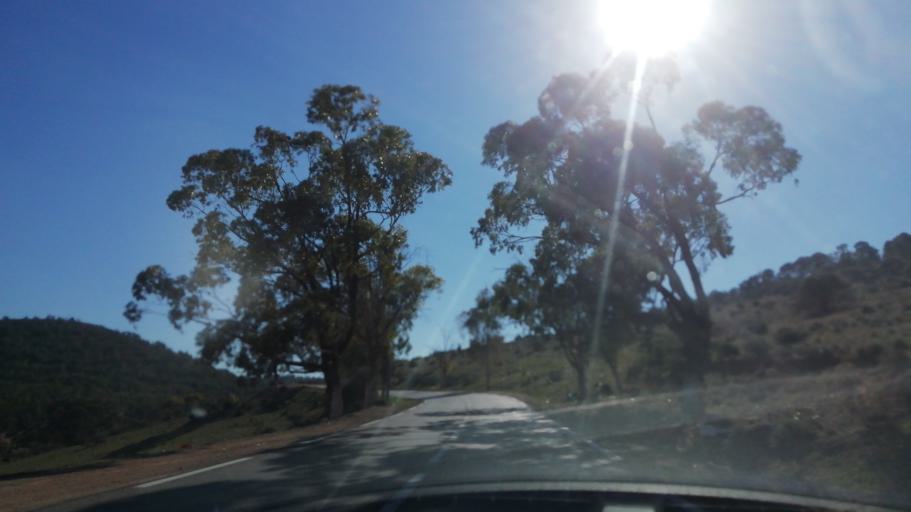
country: DZ
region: Tlemcen
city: Beni Mester
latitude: 34.8227
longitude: -1.6374
